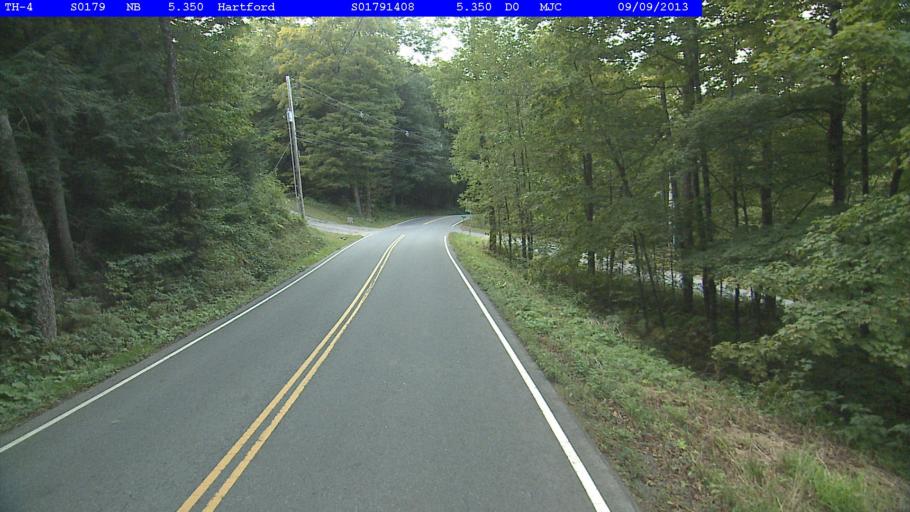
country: US
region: Vermont
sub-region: Windsor County
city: White River Junction
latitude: 43.7054
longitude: -72.4206
